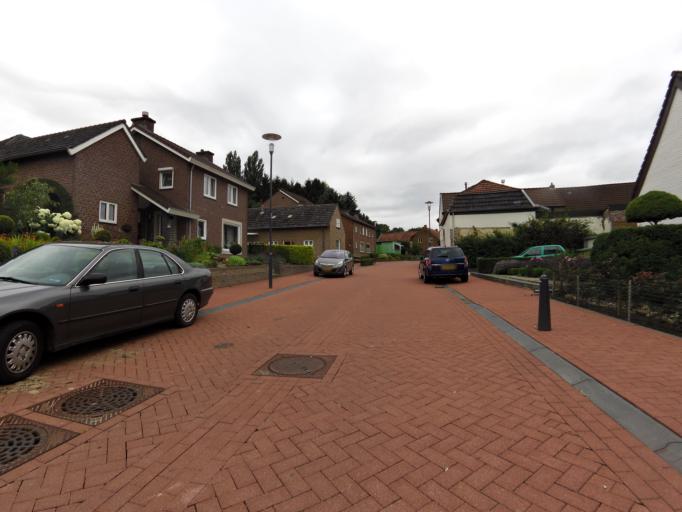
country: NL
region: Limburg
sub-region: Gemeente Nuth
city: Nuth
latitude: 50.9188
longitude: 5.8657
